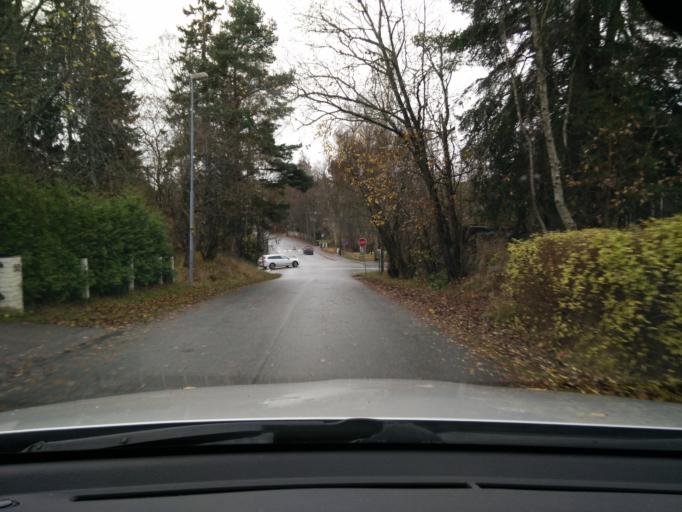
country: SE
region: Stockholm
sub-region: Sollentuna Kommun
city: Sollentuna
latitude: 59.4608
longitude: 17.9481
